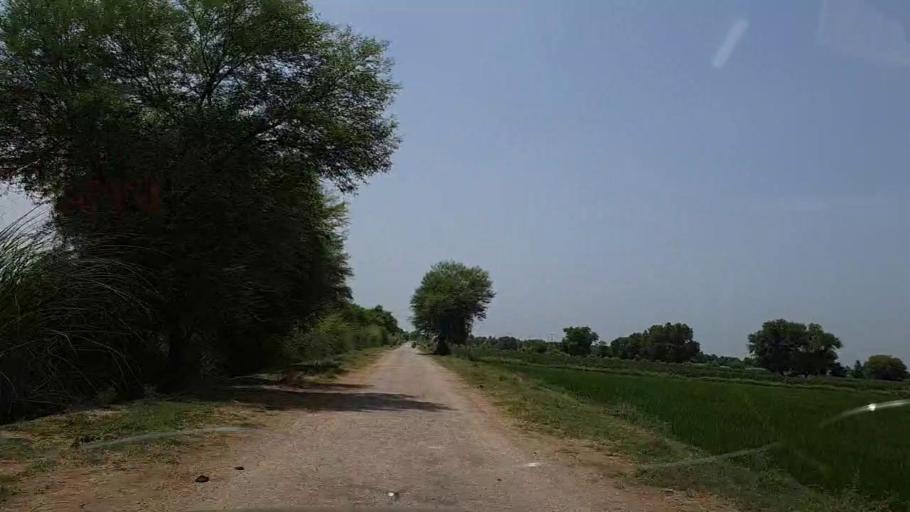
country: PK
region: Sindh
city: Khanpur
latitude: 27.8007
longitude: 69.4844
